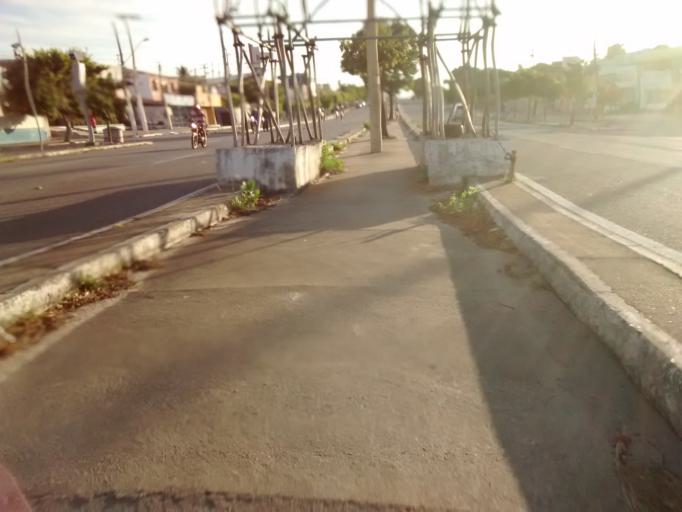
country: BR
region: Ceara
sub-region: Fortaleza
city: Fortaleza
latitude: -3.7379
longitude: -38.5791
